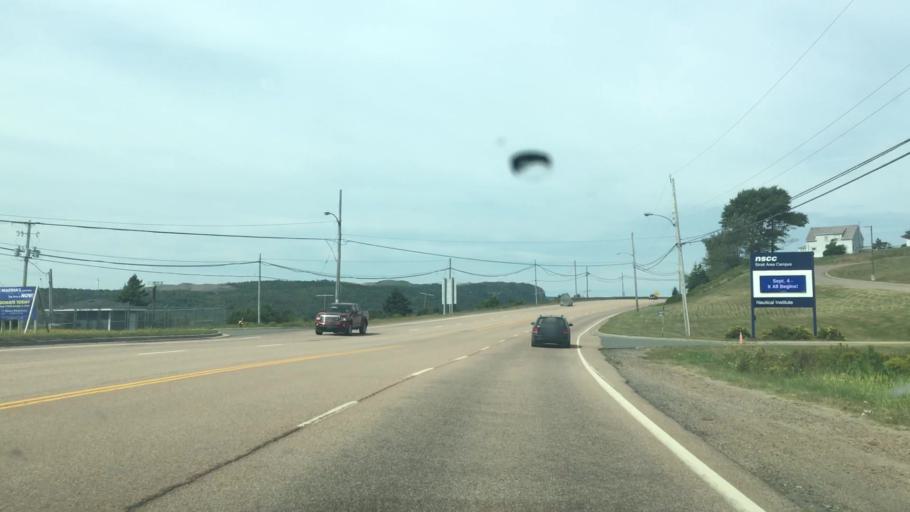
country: CA
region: Nova Scotia
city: Port Hawkesbury
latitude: 45.6255
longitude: -61.3692
